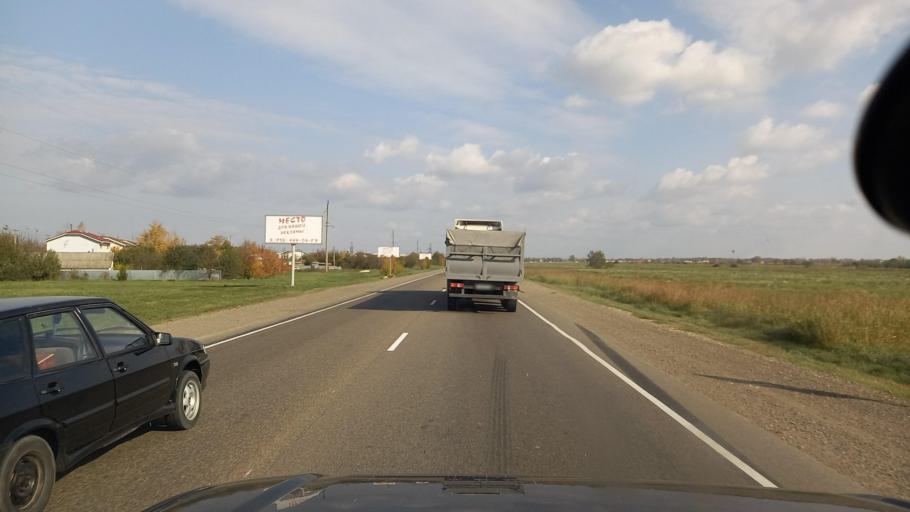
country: RU
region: Krasnodarskiy
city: Abinsk
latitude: 44.8511
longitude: 38.1843
